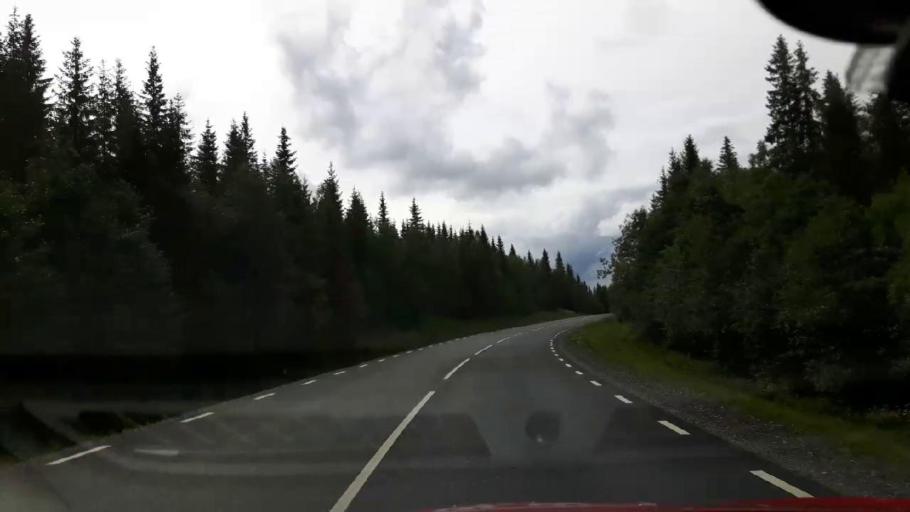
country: NO
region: Nord-Trondelag
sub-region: Lierne
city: Sandvika
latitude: 64.6419
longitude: 14.1403
